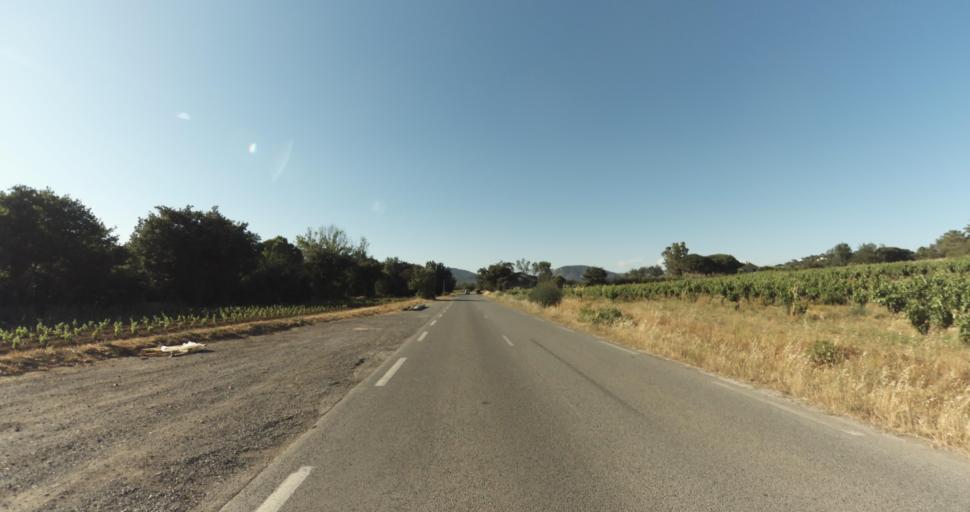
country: FR
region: Provence-Alpes-Cote d'Azur
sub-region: Departement du Var
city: Gassin
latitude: 43.2462
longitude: 6.5945
